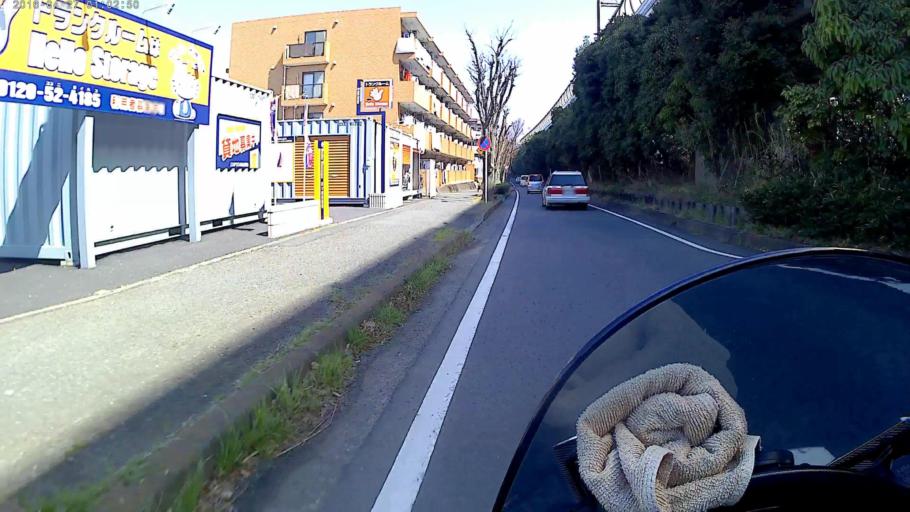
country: JP
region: Kanagawa
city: Chigasaki
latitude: 35.3469
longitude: 139.4319
